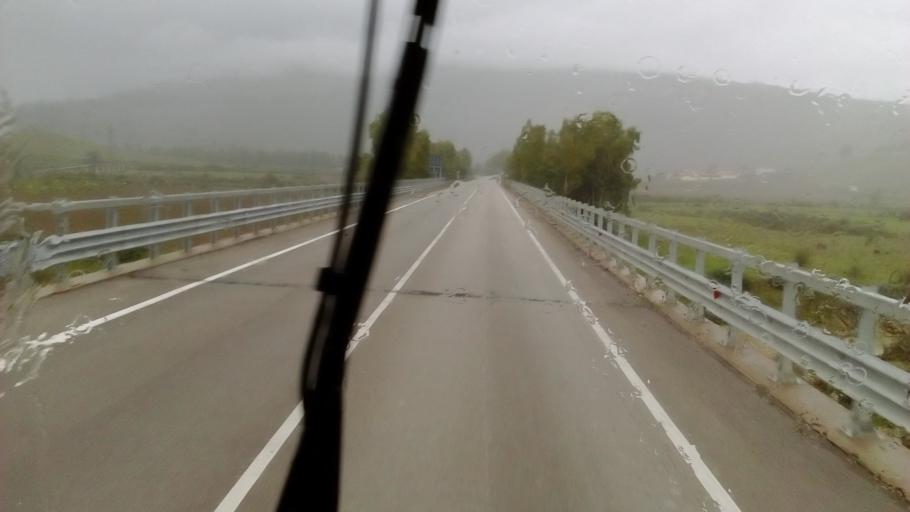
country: IT
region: Sicily
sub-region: Enna
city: Villarosa
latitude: 37.5308
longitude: 14.1295
